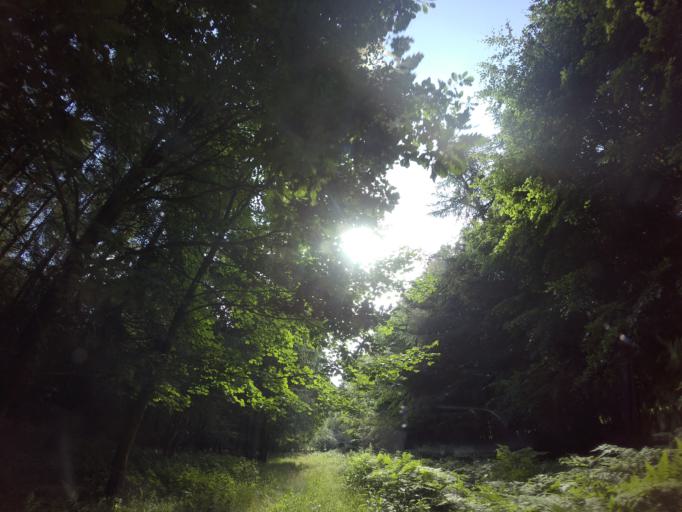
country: PL
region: West Pomeranian Voivodeship
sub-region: Powiat choszczenski
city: Krzecin
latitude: 52.9952
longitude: 15.5185
